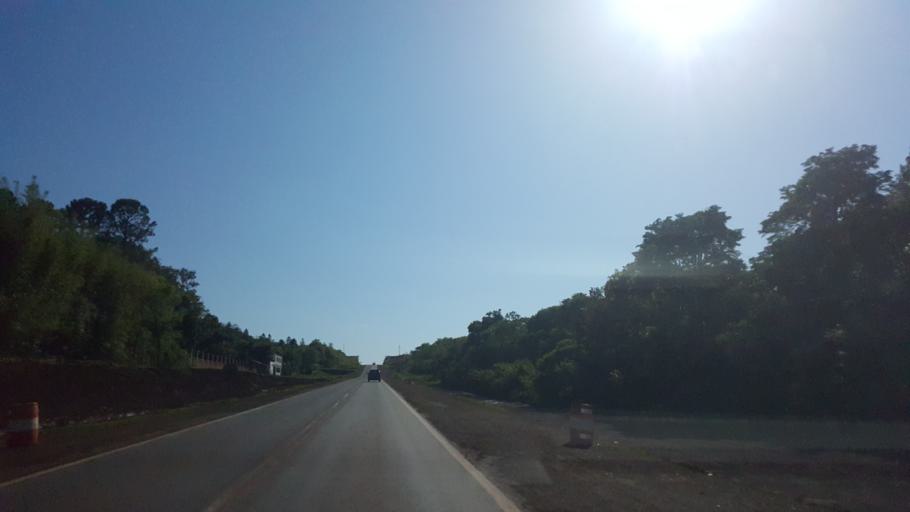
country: AR
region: Misiones
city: Santa Ana
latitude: -27.3738
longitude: -55.5708
